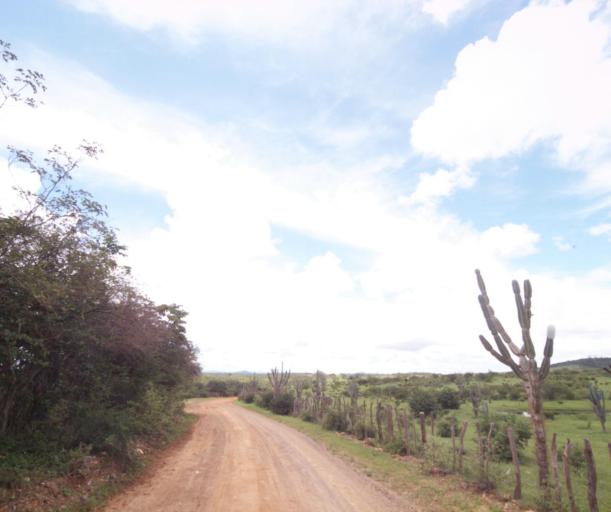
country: BR
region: Bahia
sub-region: Tanhacu
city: Tanhacu
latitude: -14.1892
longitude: -41.0801
